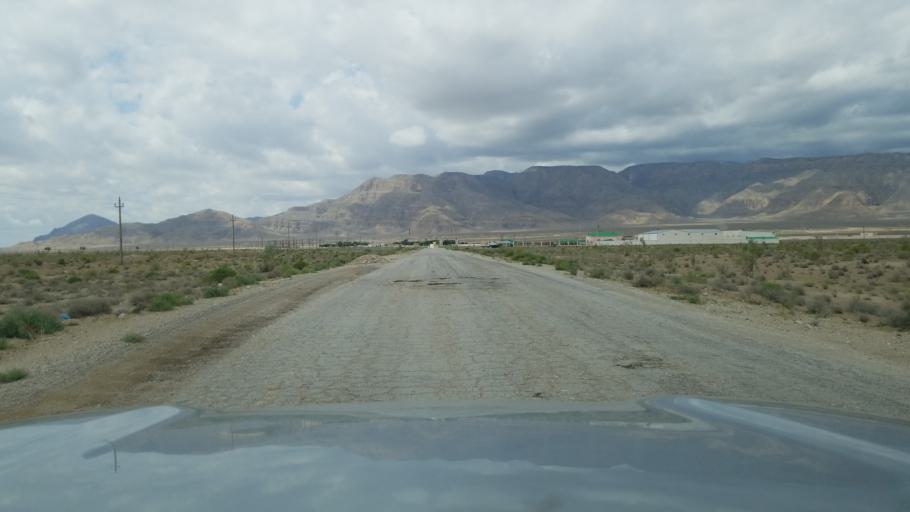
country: TM
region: Balkan
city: Balkanabat
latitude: 39.4710
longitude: 54.4637
